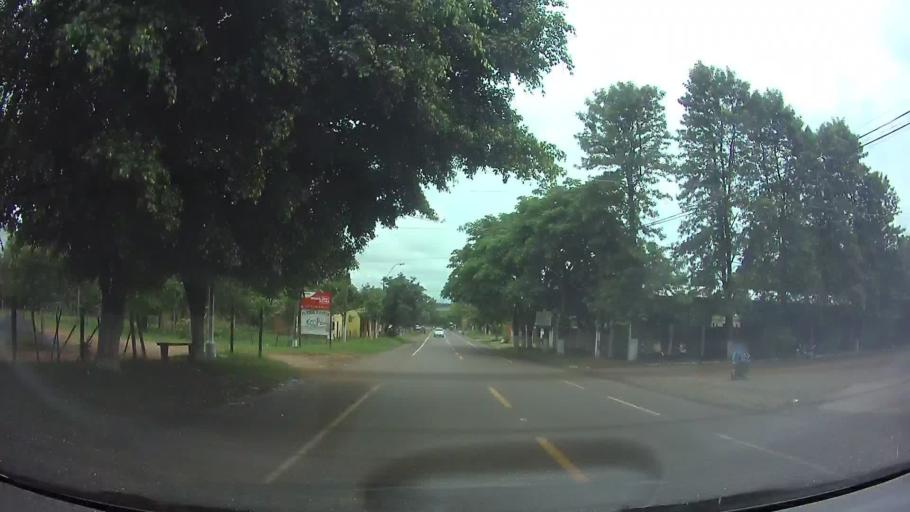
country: PY
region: Paraguari
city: Acahay
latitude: -25.9095
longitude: -57.1146
